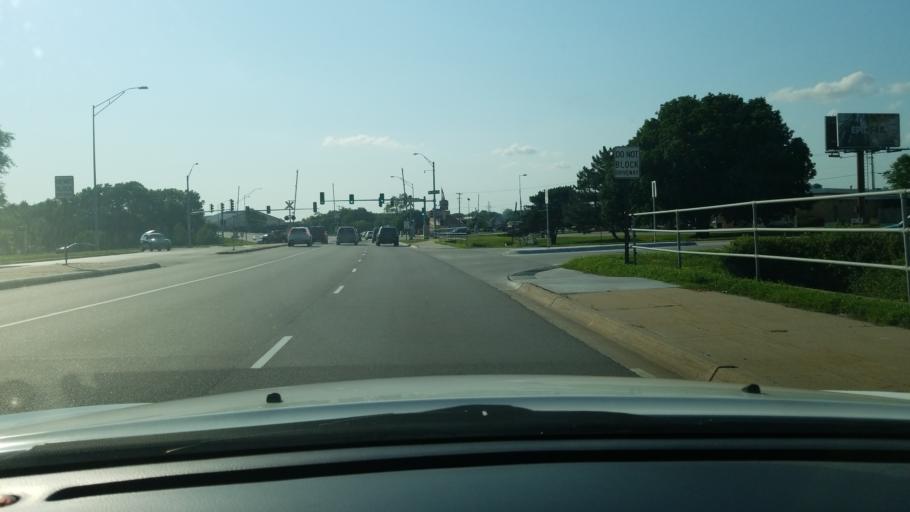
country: US
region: Nebraska
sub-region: Lancaster County
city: Lincoln
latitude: 40.7541
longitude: -96.6433
